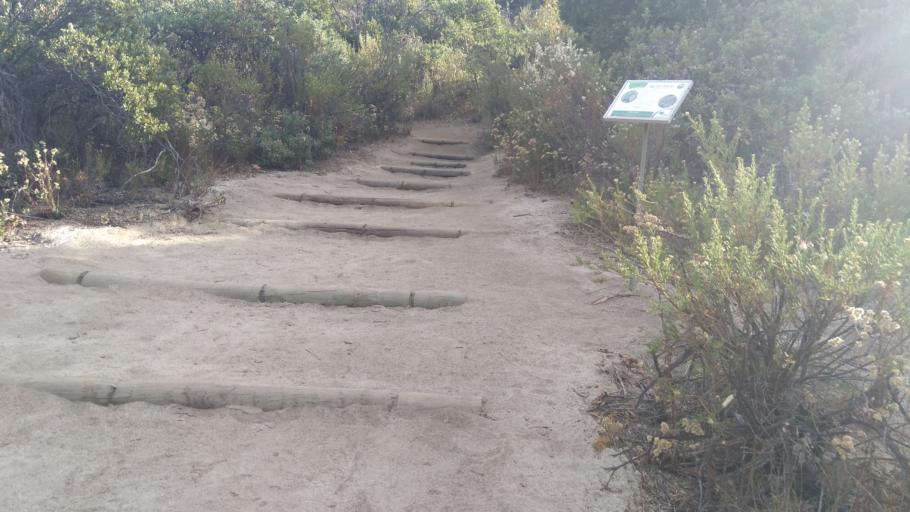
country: CL
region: Santiago Metropolitan
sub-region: Provincia de Cordillera
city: Puente Alto
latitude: -33.7235
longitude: -70.4805
